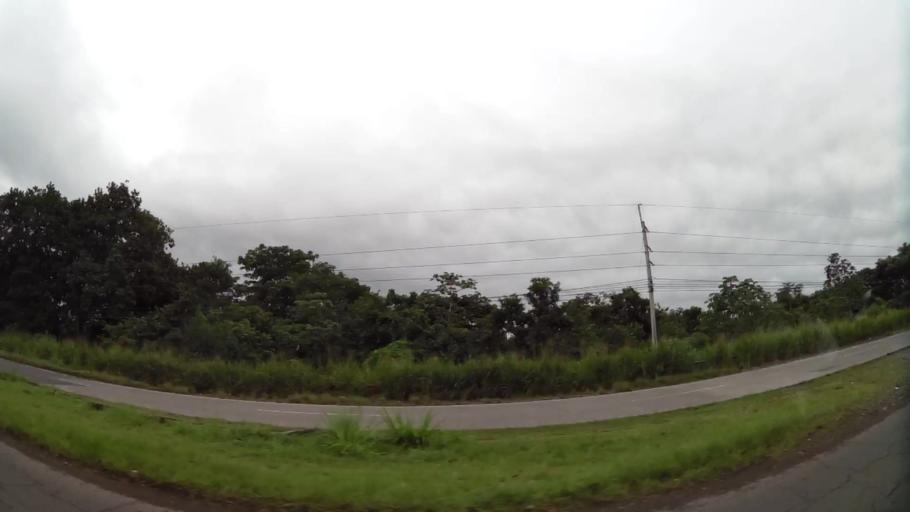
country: PA
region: Chiriqui
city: Tijera
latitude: 8.4719
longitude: -82.5423
